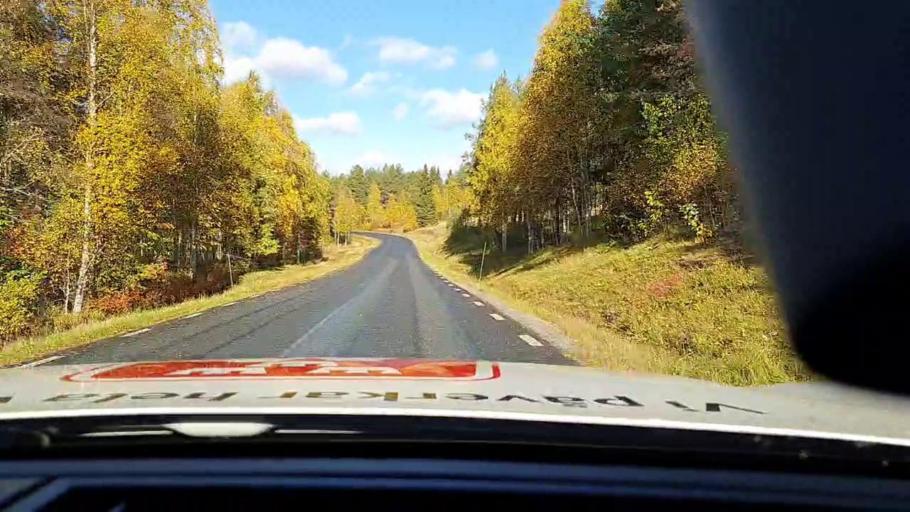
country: SE
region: Vaesterbotten
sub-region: Skelleftea Kommun
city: Langsele
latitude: 65.0078
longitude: 20.0885
